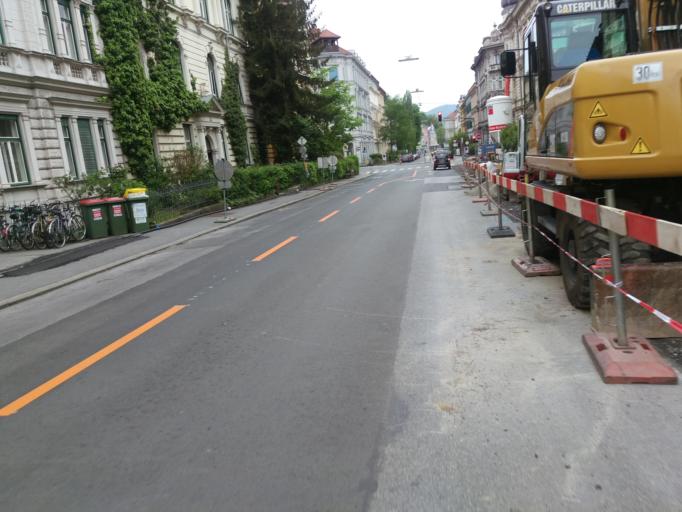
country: AT
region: Styria
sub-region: Graz Stadt
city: Graz
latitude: 47.0799
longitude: 15.4431
